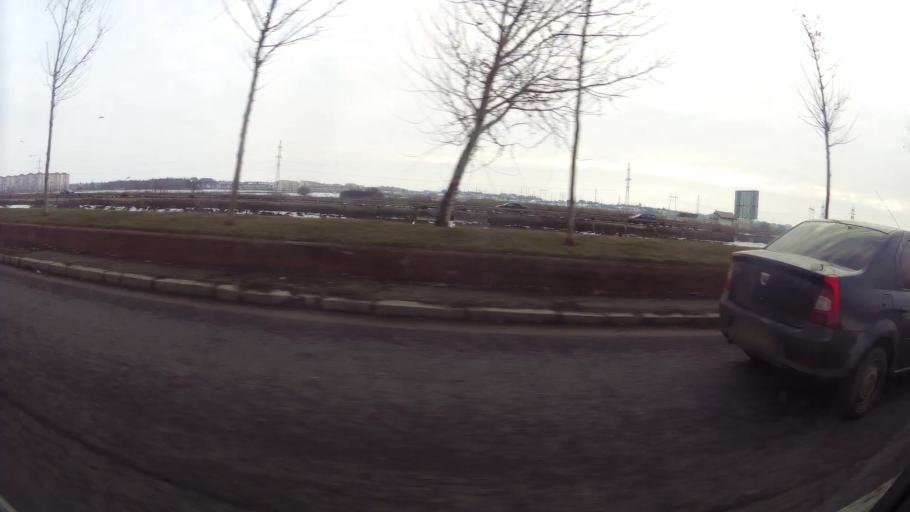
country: RO
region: Ilfov
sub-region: Comuna Popesti-Leordeni
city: Popesti-Leordeni
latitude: 44.3947
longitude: 26.1896
